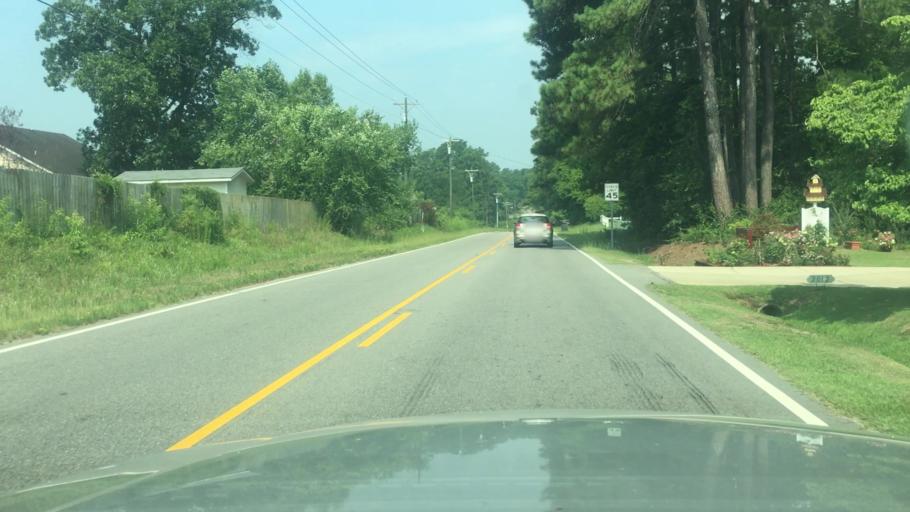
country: US
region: North Carolina
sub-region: Cumberland County
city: Hope Mills
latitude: 35.0010
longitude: -78.9561
